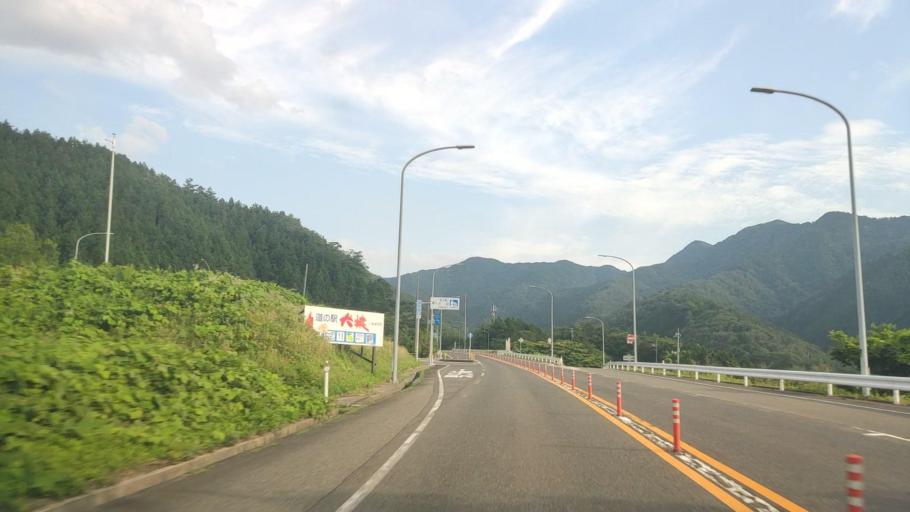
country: JP
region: Tottori
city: Kurayoshi
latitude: 35.3300
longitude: 133.7550
